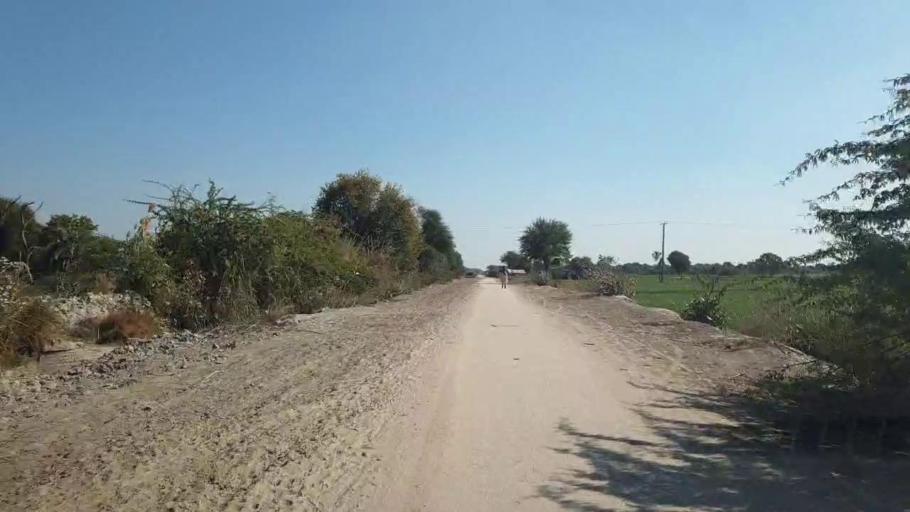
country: PK
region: Sindh
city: Shahpur Chakar
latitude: 26.1359
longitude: 68.6632
